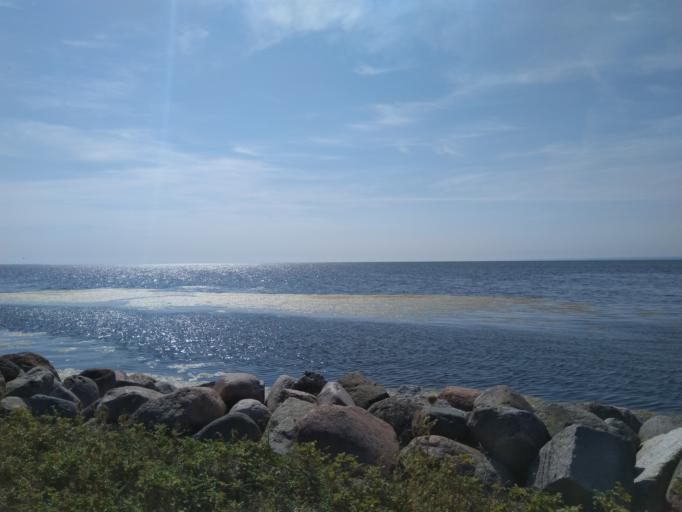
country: PL
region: Pomeranian Voivodeship
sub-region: Powiat pucki
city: Jastarnia
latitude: 54.7271
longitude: 18.6011
